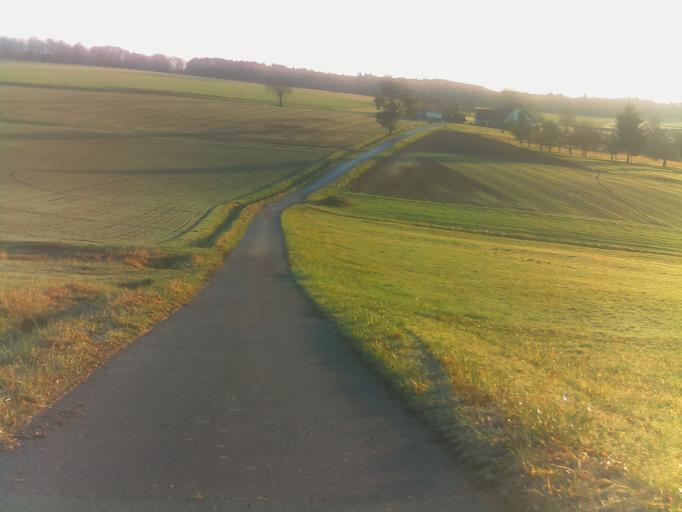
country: DE
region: Bavaria
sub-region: Regierungsbezirk Unterfranken
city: Miltenberg
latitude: 49.6613
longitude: 9.2761
